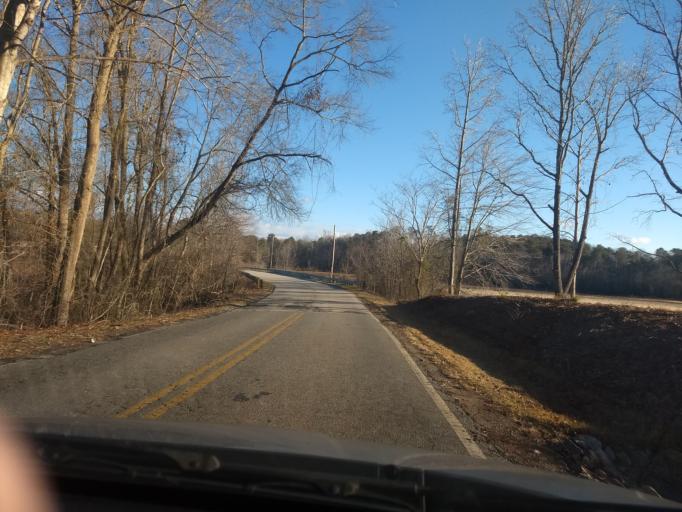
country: US
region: South Carolina
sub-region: Greenville County
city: Greer
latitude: 35.0144
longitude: -82.2068
